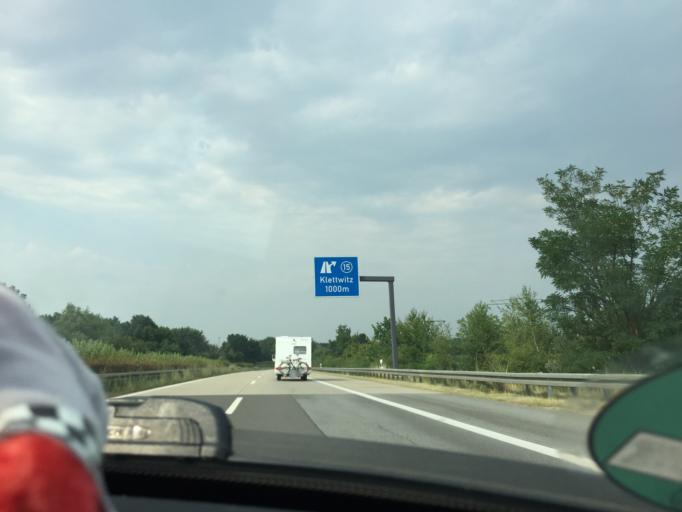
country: DE
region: Brandenburg
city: Schipkau
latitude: 51.5230
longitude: 13.9054
